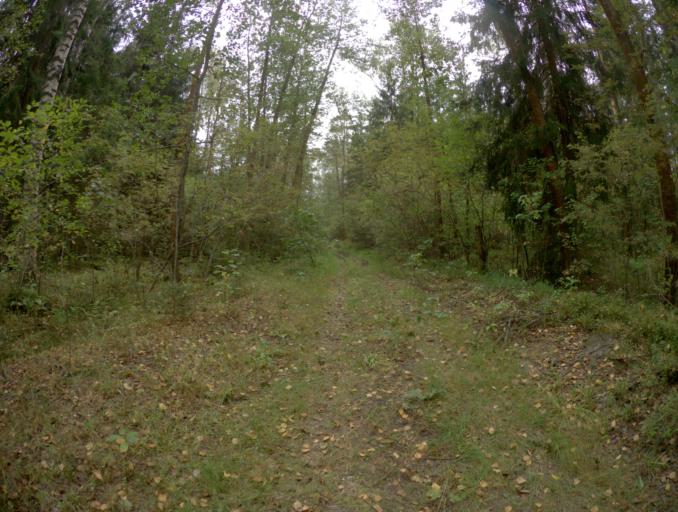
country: RU
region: Vladimir
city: Urshel'skiy
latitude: 55.8234
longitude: 40.2765
